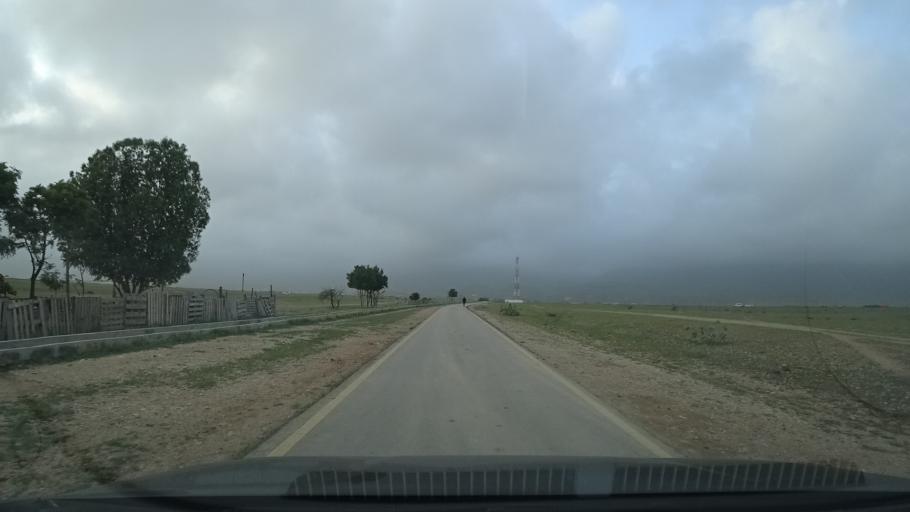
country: OM
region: Zufar
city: Salalah
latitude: 17.0824
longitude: 54.2318
